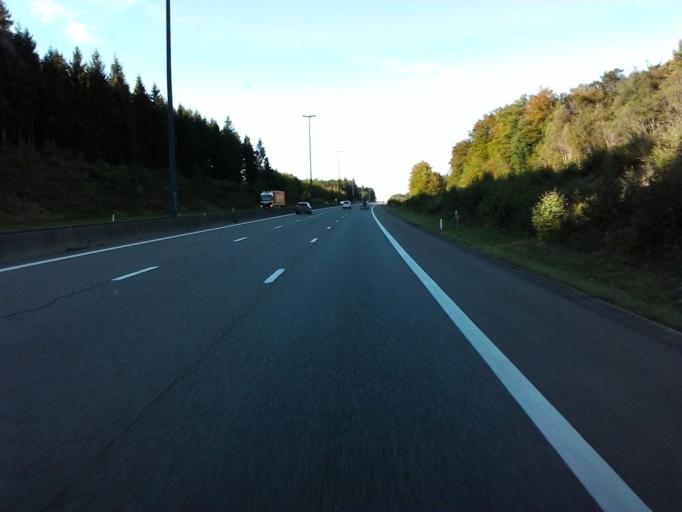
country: BE
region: Wallonia
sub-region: Province du Luxembourg
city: Houffalize
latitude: 50.1893
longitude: 5.7805
